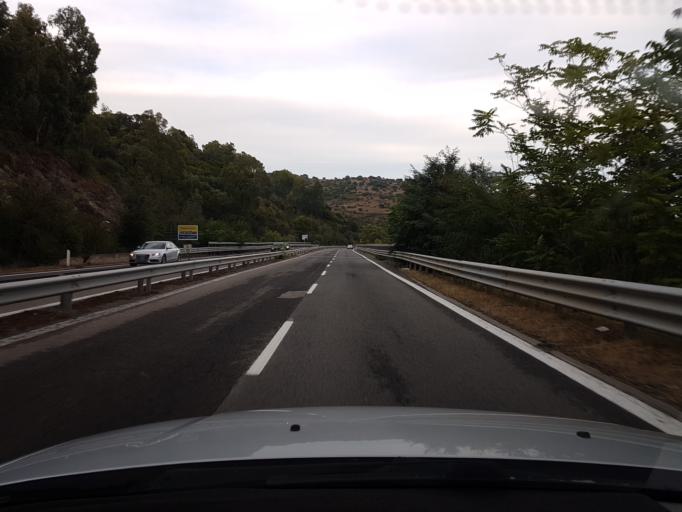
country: IT
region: Sardinia
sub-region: Provincia di Nuoro
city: Nuoro
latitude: 40.3363
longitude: 9.3000
